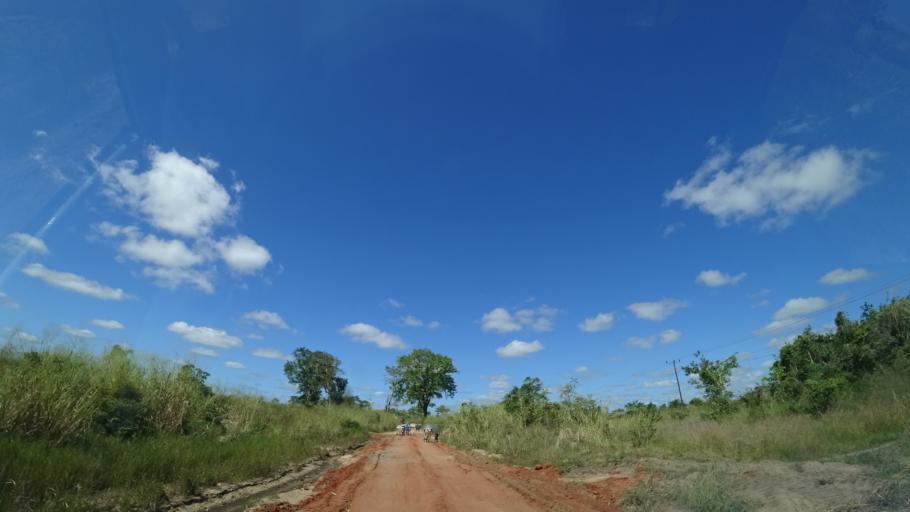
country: MZ
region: Sofala
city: Dondo
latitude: -19.2760
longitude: 34.6809
